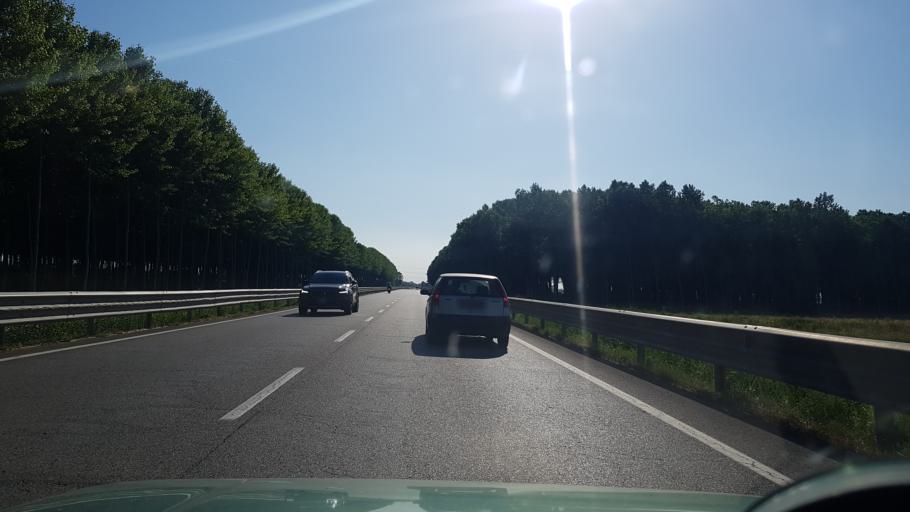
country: IT
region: Friuli Venezia Giulia
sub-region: Provincia di Udine
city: Torviscosa
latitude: 45.8289
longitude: 13.2628
